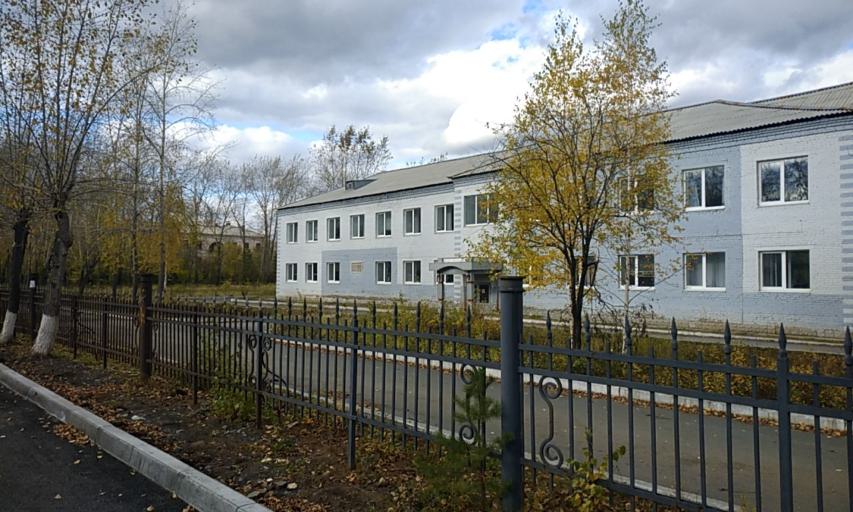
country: RU
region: Sverdlovsk
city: Krasnoural'sk
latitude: 58.3577
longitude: 60.0345
